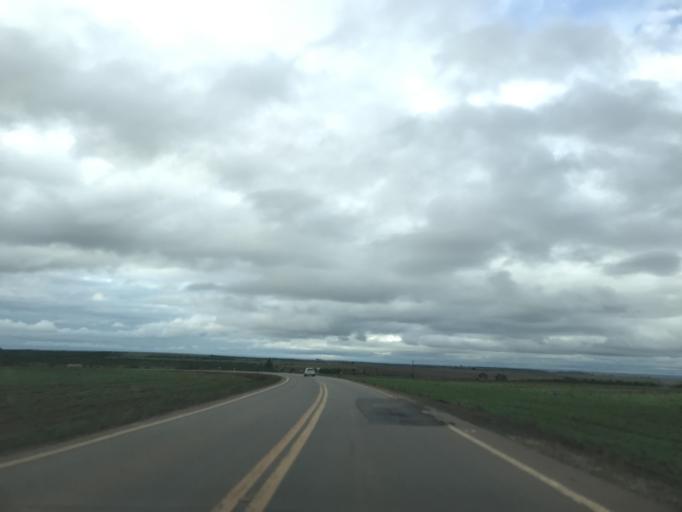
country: BR
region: Goias
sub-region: Luziania
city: Luziania
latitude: -16.4958
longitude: -48.2013
